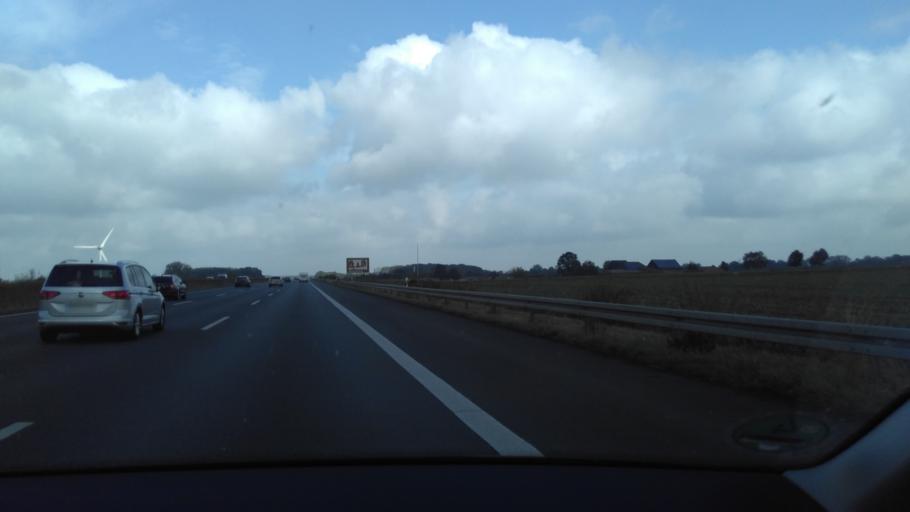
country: DE
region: North Rhine-Westphalia
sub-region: Regierungsbezirk Munster
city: Beckum
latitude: 51.7300
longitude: 7.9837
